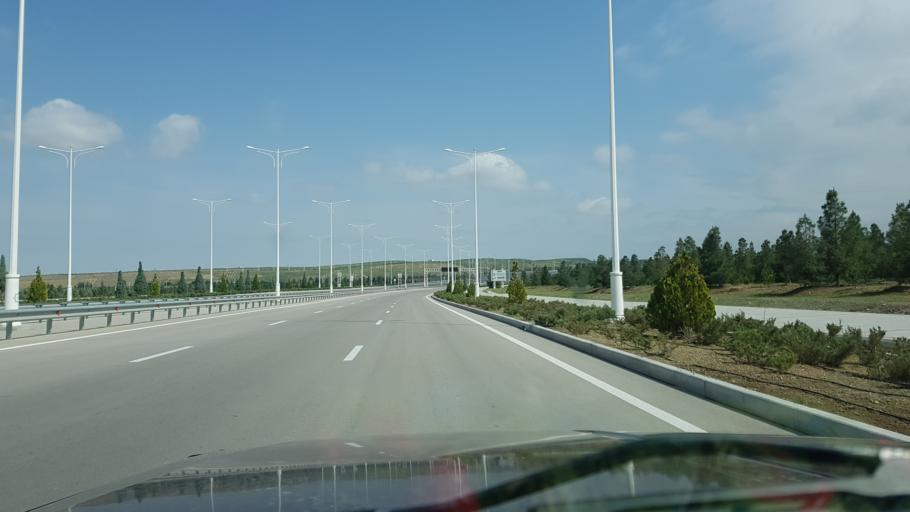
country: TM
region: Ahal
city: Ashgabat
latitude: 37.8637
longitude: 58.3664
